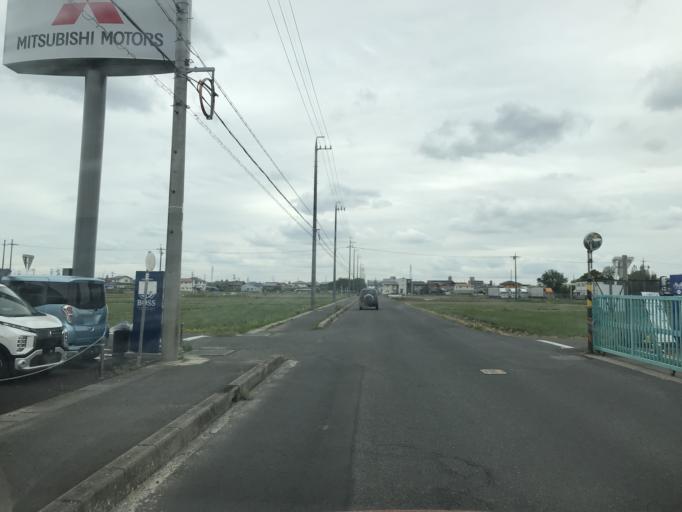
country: JP
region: Aichi
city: Kasugai
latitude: 35.2693
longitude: 136.9681
